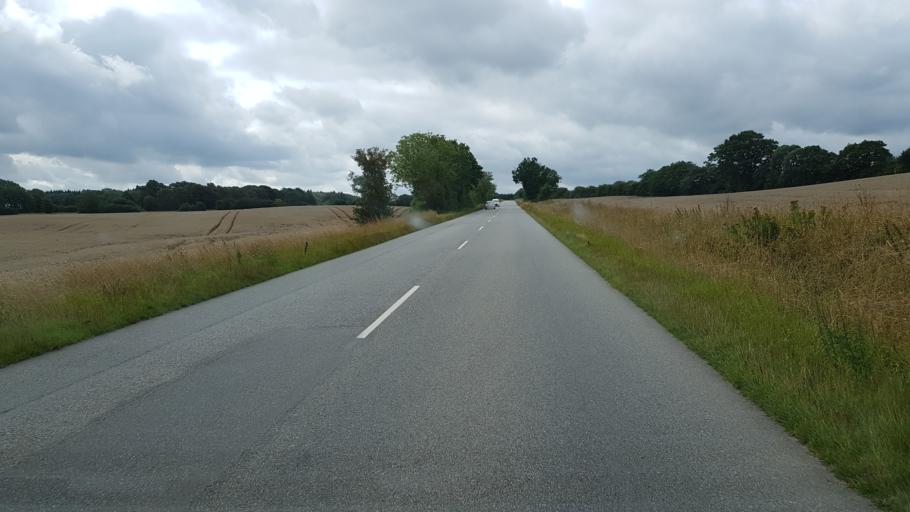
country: DK
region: South Denmark
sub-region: Kolding Kommune
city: Kolding
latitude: 55.4767
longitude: 9.4062
